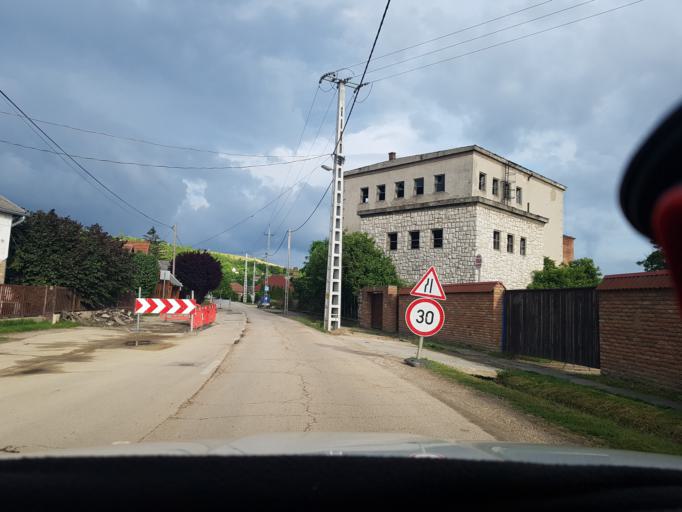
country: HU
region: Komarom-Esztergom
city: Sarisap
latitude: 47.6811
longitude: 18.6746
